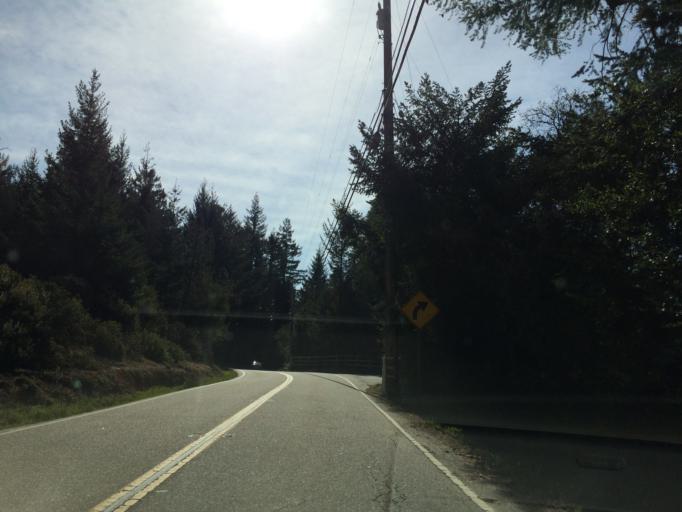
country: US
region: California
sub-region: Santa Cruz County
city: Felton
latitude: 37.0431
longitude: -122.1078
